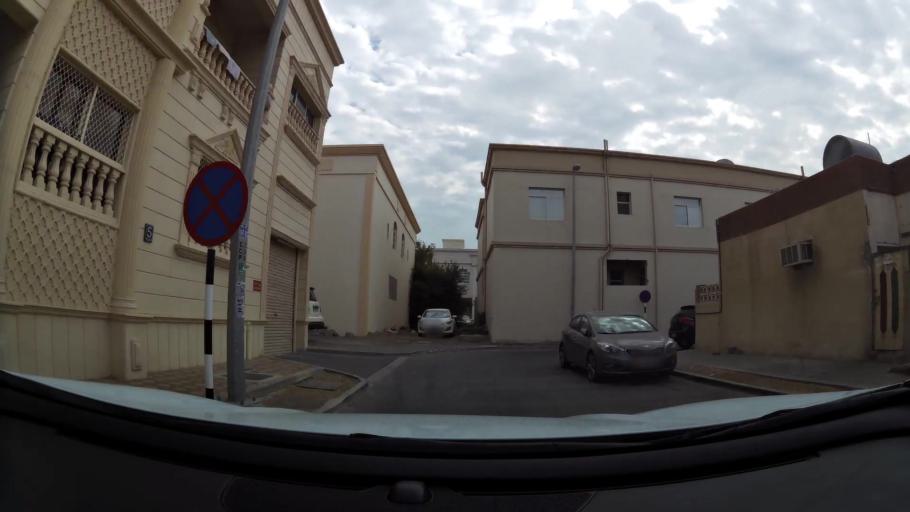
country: AE
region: Abu Dhabi
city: Al Ain
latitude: 24.2228
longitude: 55.7472
